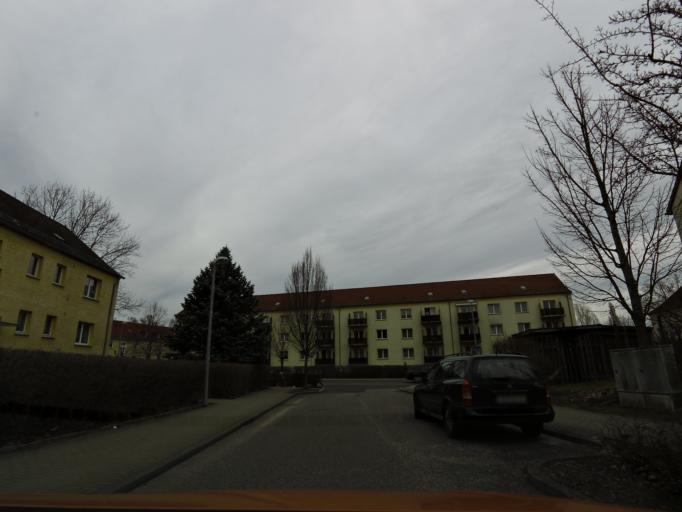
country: DE
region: Brandenburg
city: Belzig
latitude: 52.1414
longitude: 12.6014
